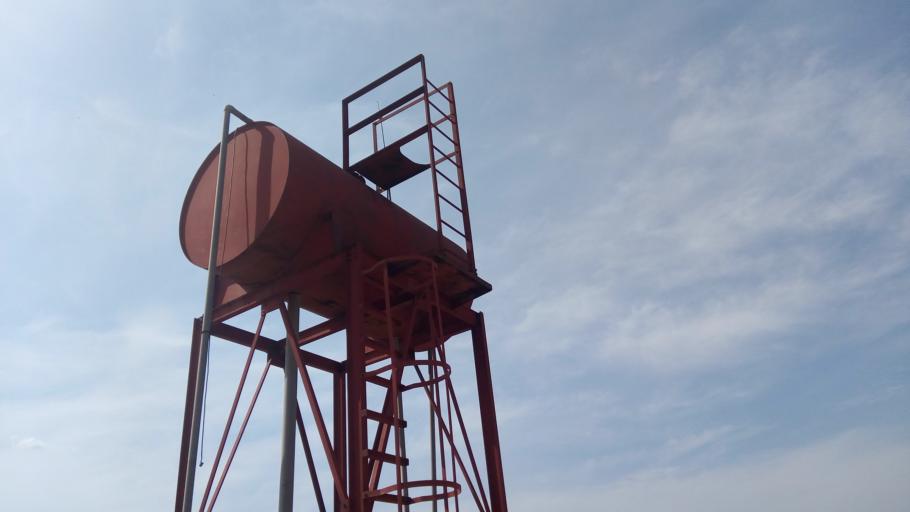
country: ML
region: Koulikoro
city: Kangaba
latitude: 11.6795
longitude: -8.7137
